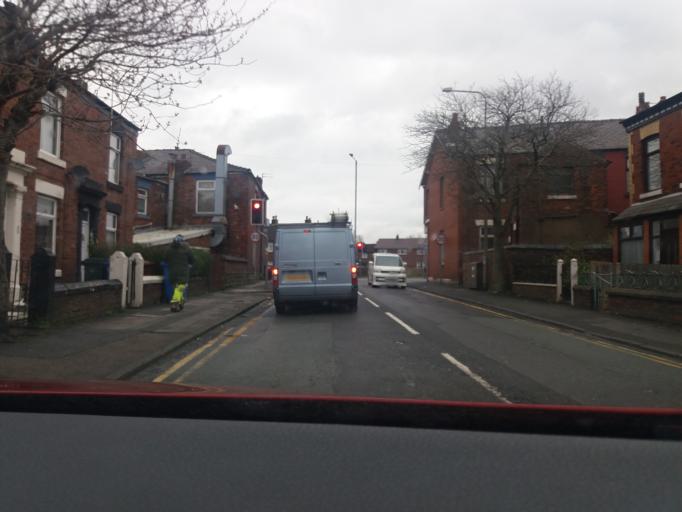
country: GB
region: England
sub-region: Lancashire
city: Chorley
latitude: 53.6462
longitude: -2.6266
